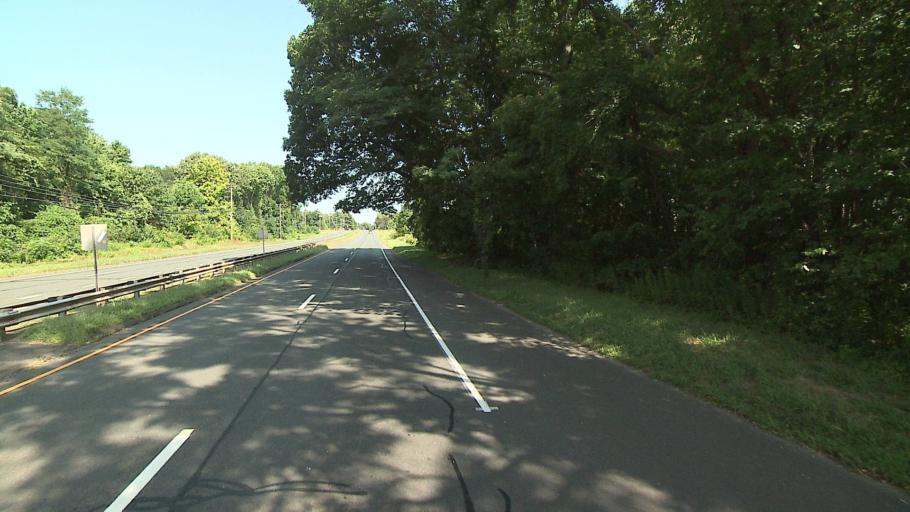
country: US
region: Connecticut
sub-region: Hartford County
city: South Windsor
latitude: 41.8536
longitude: -72.6004
